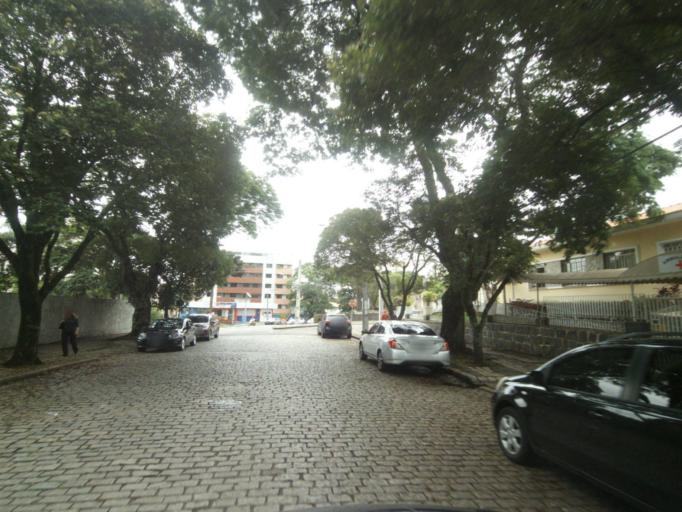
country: BR
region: Parana
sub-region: Curitiba
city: Curitiba
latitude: -25.4163
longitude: -49.2641
